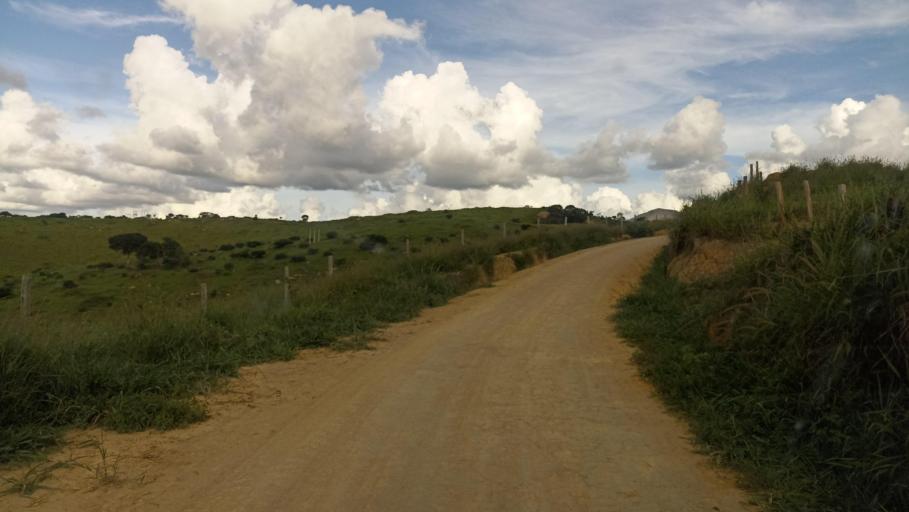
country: BR
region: Minas Gerais
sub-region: Almenara
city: Almenara
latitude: -16.5482
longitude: -40.4545
